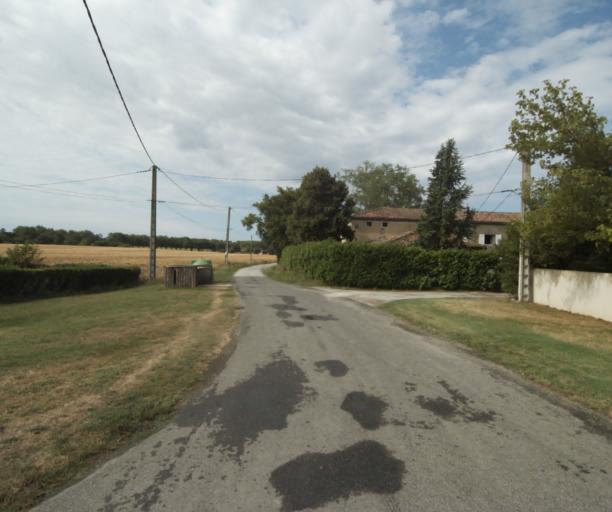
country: FR
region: Midi-Pyrenees
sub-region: Departement de la Haute-Garonne
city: Revel
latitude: 43.4518
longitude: 1.9628
